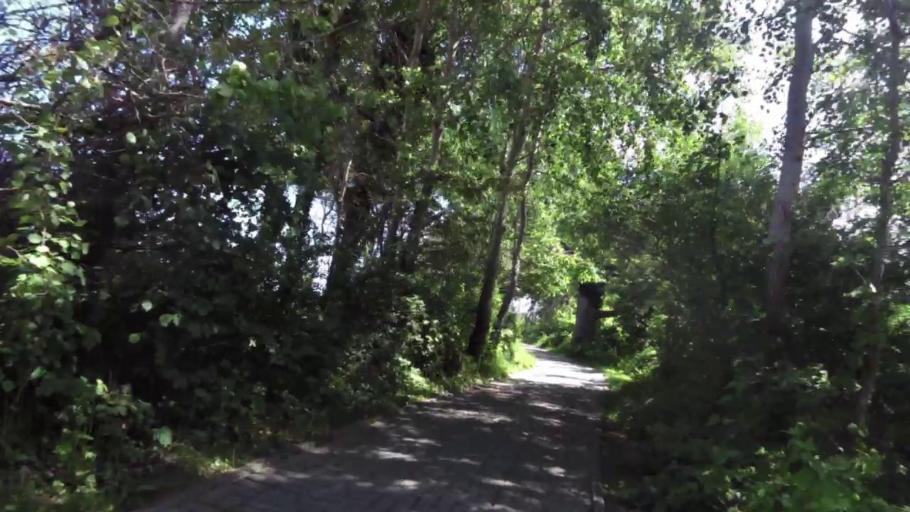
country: PL
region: West Pomeranian Voivodeship
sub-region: Powiat kolobrzeski
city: Kolobrzeg
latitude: 54.1963
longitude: 15.6414
